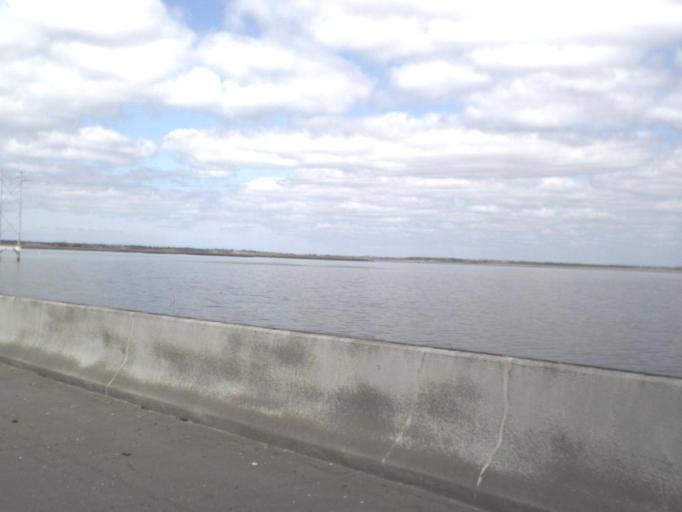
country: US
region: Florida
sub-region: Franklin County
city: Apalachicola
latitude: 29.7280
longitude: -84.9570
